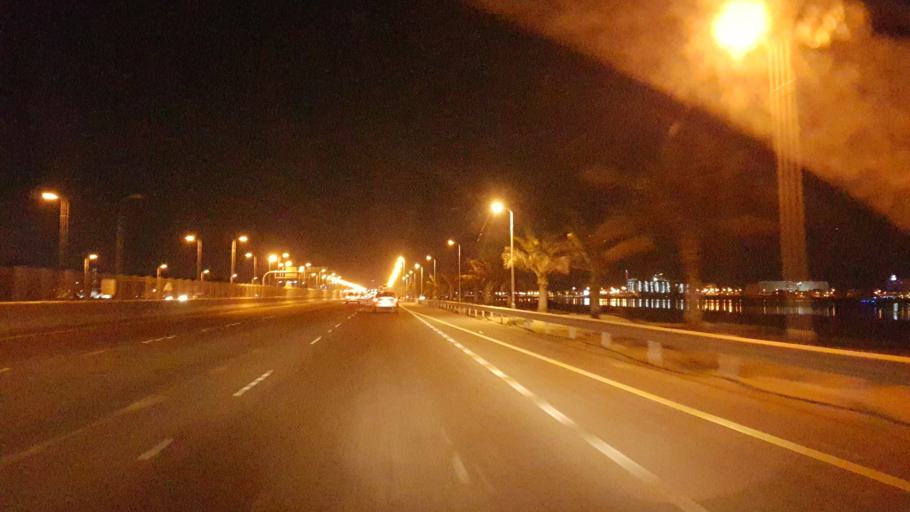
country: BH
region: Muharraq
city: Al Hadd
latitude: 26.2570
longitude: 50.6604
